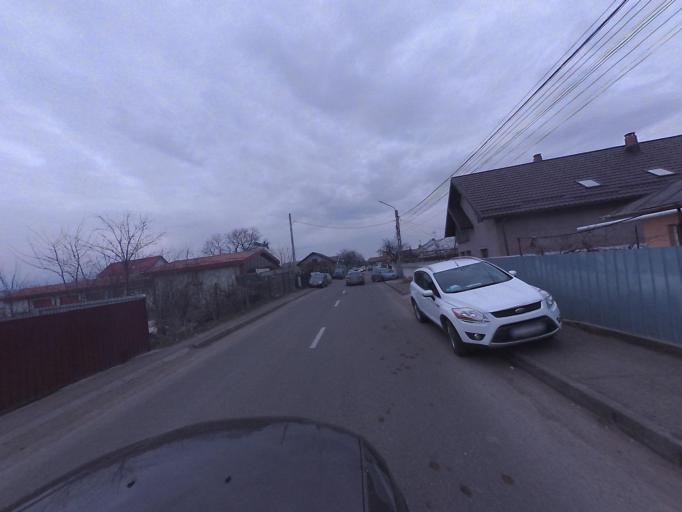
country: RO
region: Neamt
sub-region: Oras Targu Neamt
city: Targu Neamt
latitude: 47.2031
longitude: 26.3667
